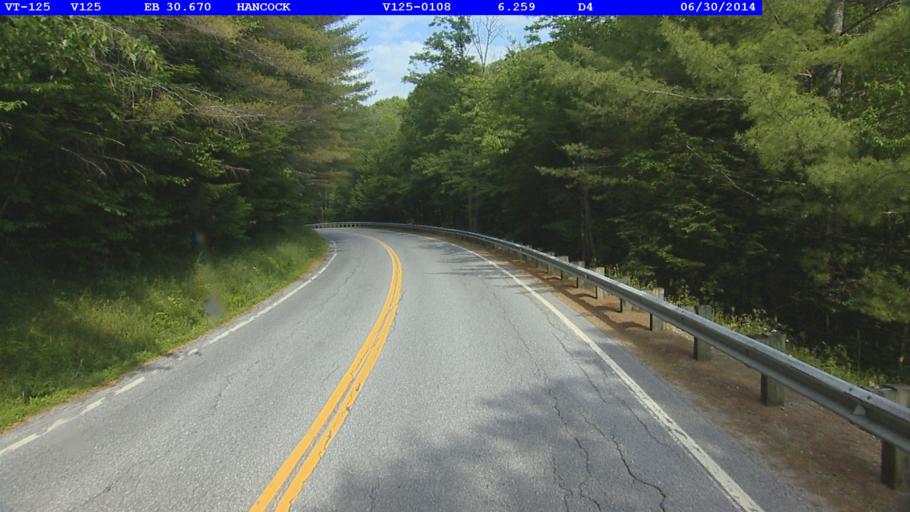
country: US
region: Vermont
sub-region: Orange County
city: Randolph
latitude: 43.9248
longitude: -72.8589
